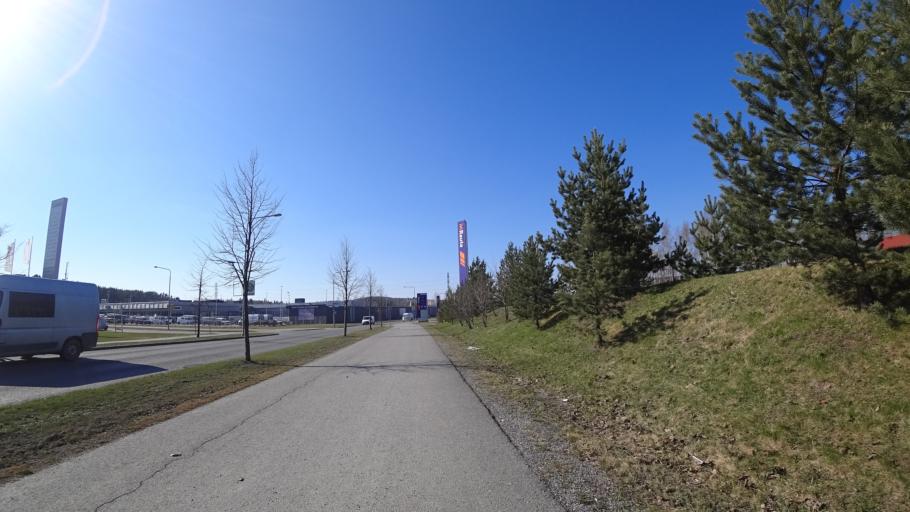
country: FI
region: Pirkanmaa
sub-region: Tampere
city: Pirkkala
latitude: 61.5192
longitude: 23.6595
